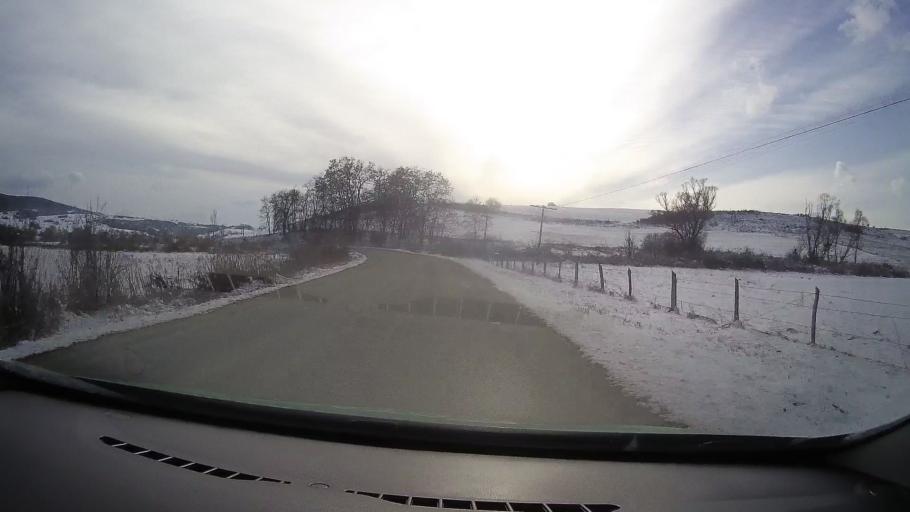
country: RO
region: Sibiu
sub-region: Comuna Iacobeni
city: Iacobeni
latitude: 46.0258
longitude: 24.7072
